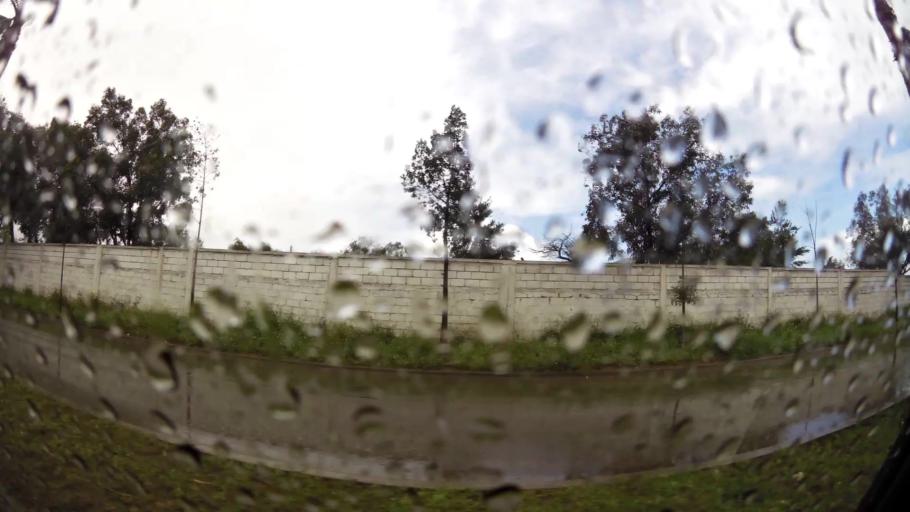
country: MA
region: Grand Casablanca
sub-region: Casablanca
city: Casablanca
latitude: 33.5496
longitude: -7.6700
